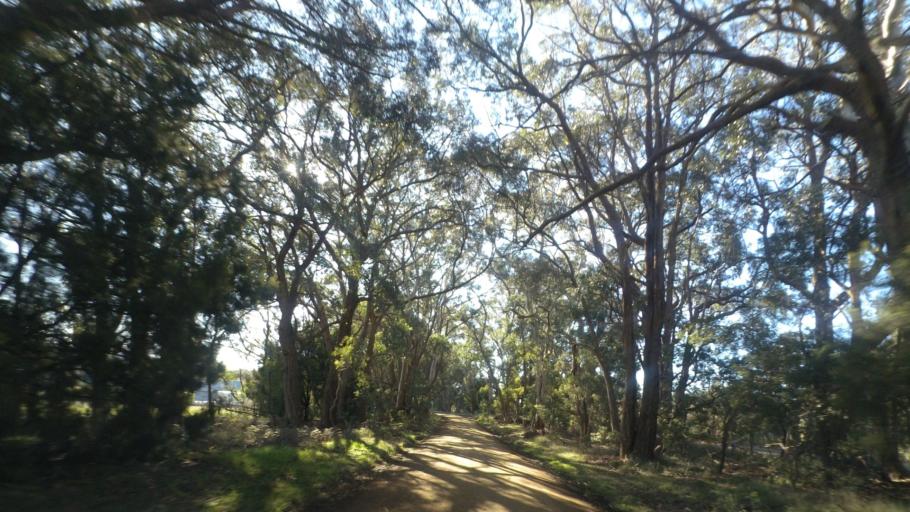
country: AU
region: Victoria
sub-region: Mount Alexander
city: Castlemaine
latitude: -37.2982
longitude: 144.3334
